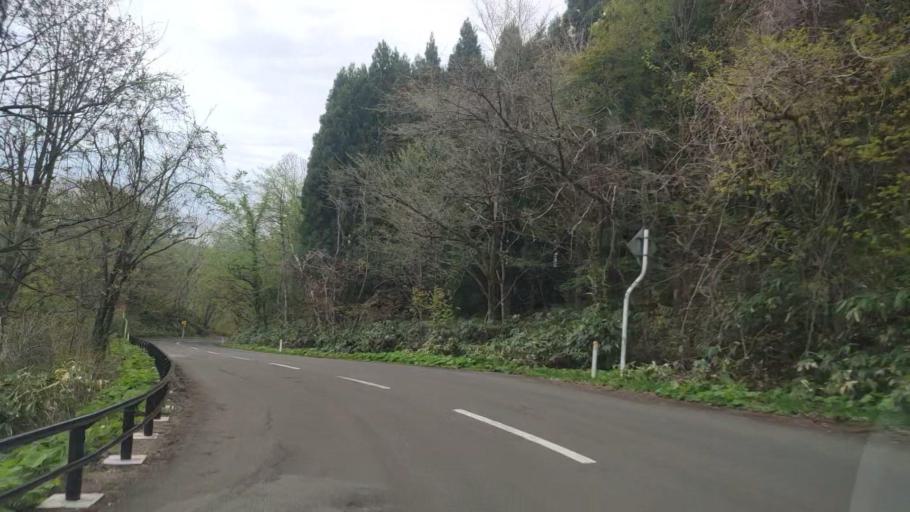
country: JP
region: Akita
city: Hanawa
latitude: 40.3742
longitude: 140.7898
